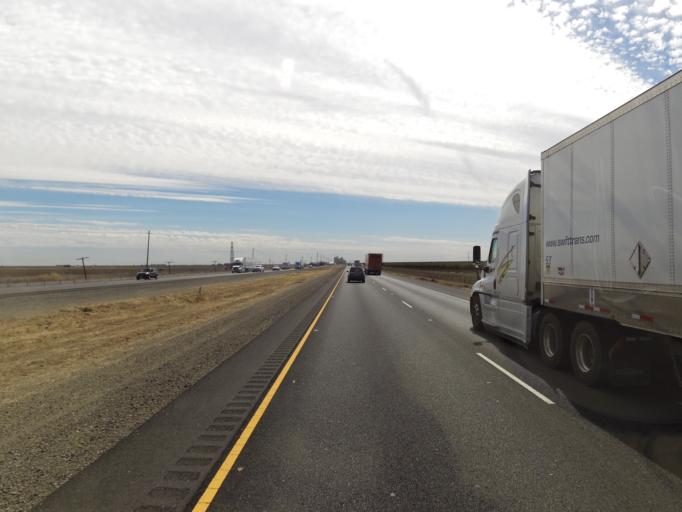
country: US
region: California
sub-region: Colusa County
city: Arbuckle
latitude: 39.0834
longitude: -122.1008
